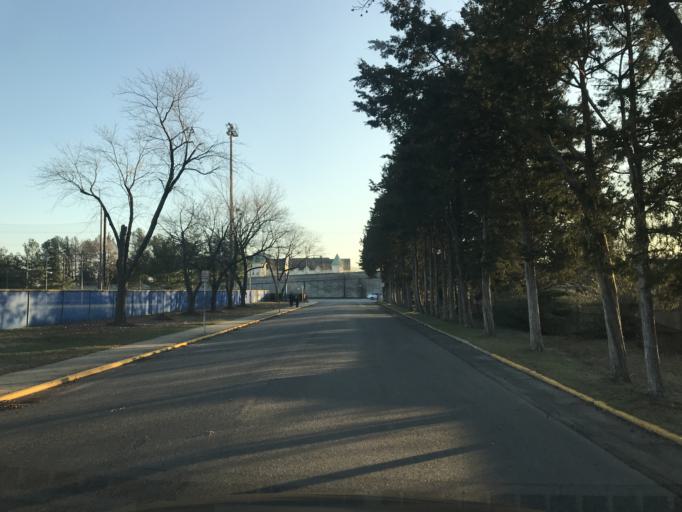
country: US
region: Virginia
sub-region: Fairfax County
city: Springfield
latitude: 38.7792
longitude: -77.1712
